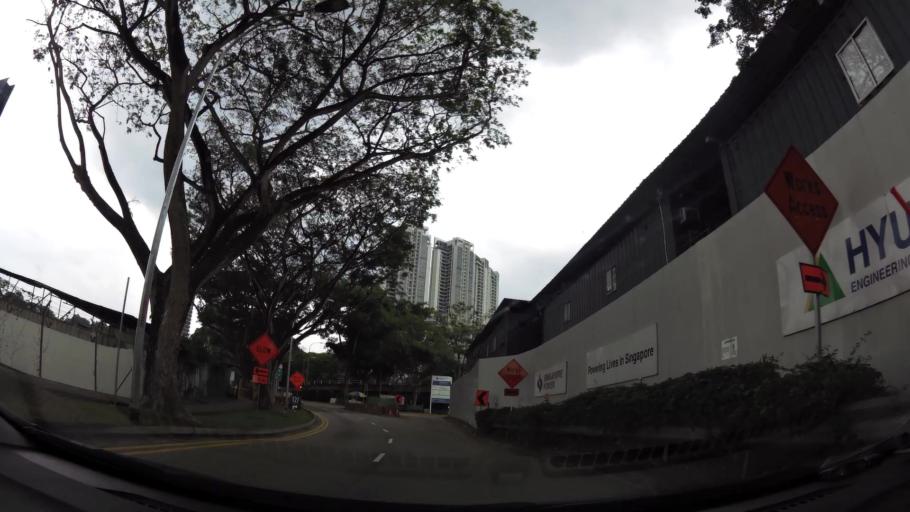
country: SG
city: Singapore
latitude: 1.3286
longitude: 103.8391
